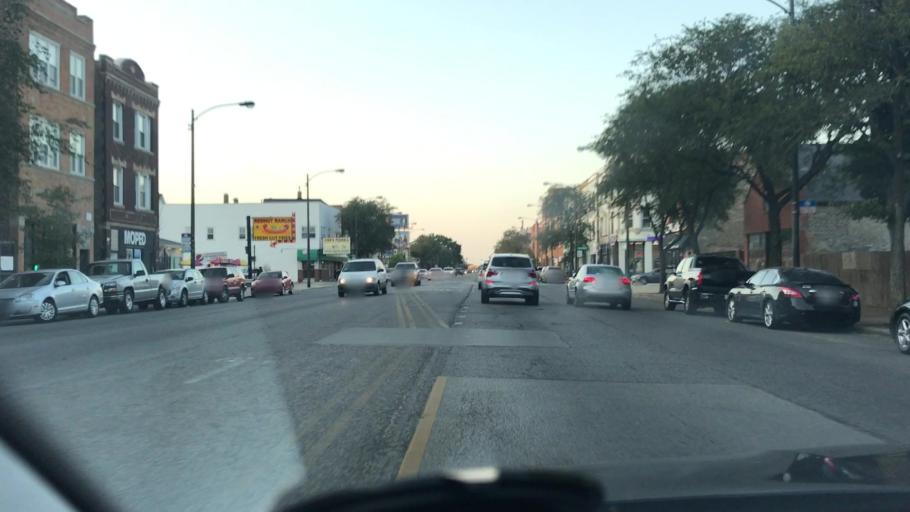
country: US
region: Illinois
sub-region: Cook County
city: Chicago
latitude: 41.9192
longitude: -87.6875
